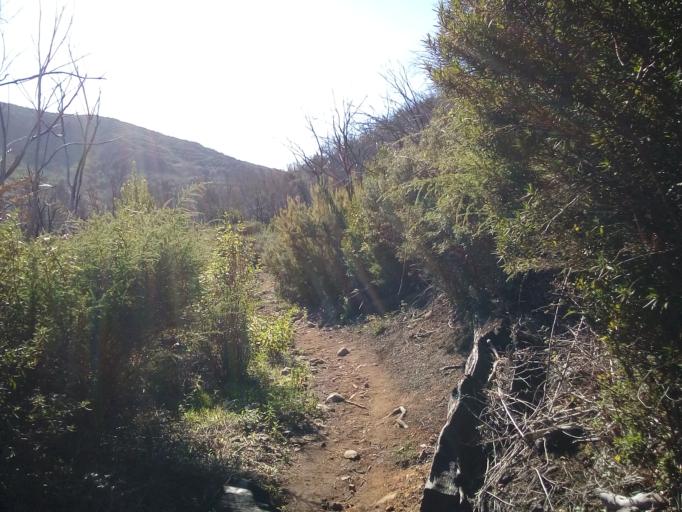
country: ES
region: Canary Islands
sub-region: Provincia de Santa Cruz de Tenerife
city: Vallehermosa
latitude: 28.1234
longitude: -17.2635
